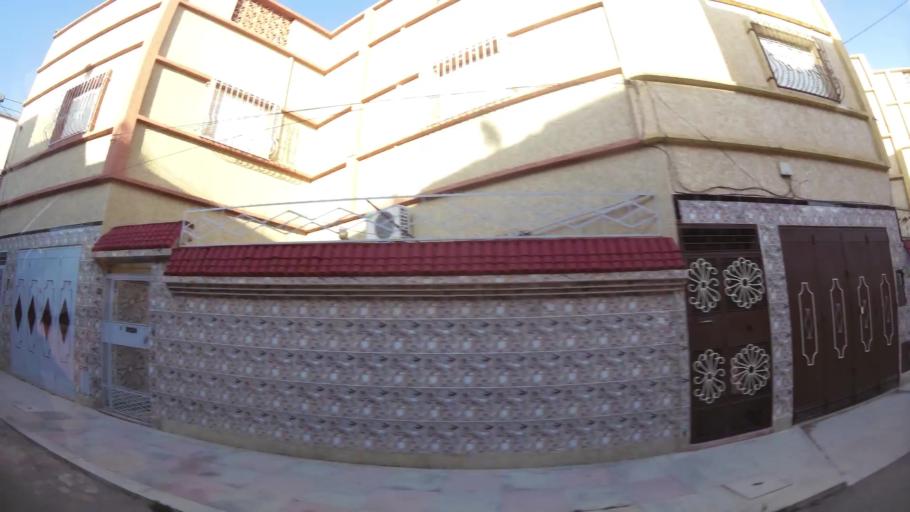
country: MA
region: Oriental
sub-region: Oujda-Angad
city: Oujda
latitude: 34.7039
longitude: -1.8978
